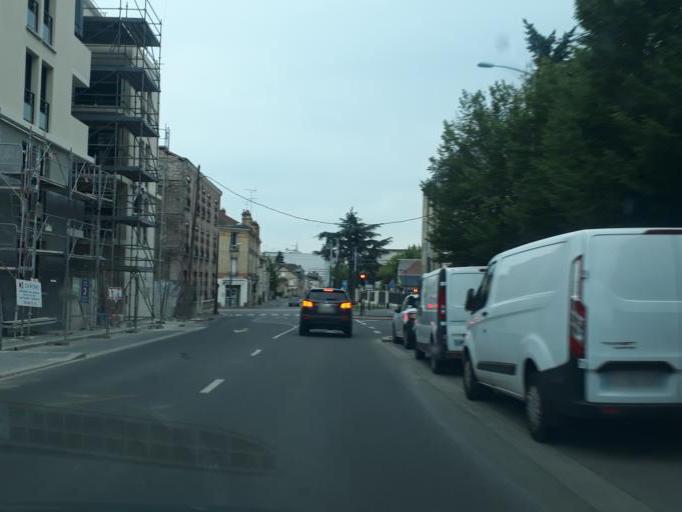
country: FR
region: Centre
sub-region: Departement du Loiret
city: Orleans
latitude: 47.9134
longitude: 1.9126
